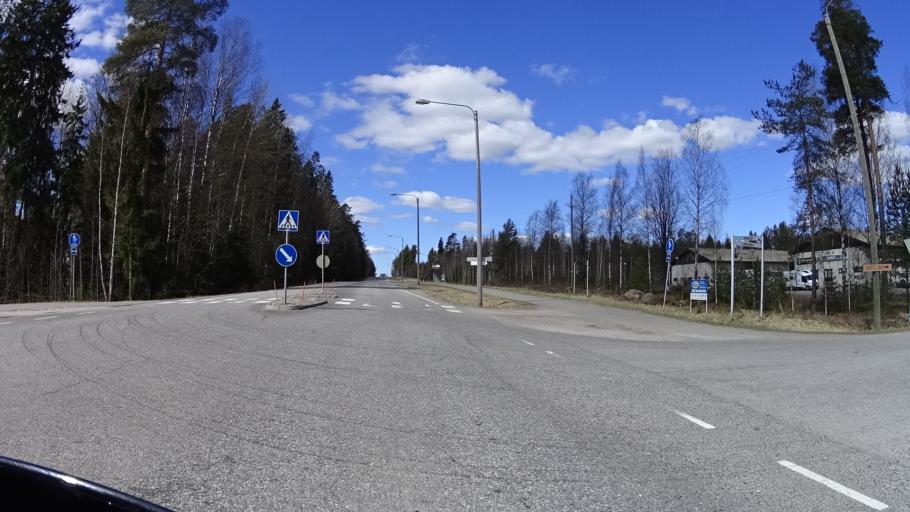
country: FI
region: Uusimaa
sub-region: Helsinki
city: Kirkkonummi
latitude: 60.2676
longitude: 24.4584
